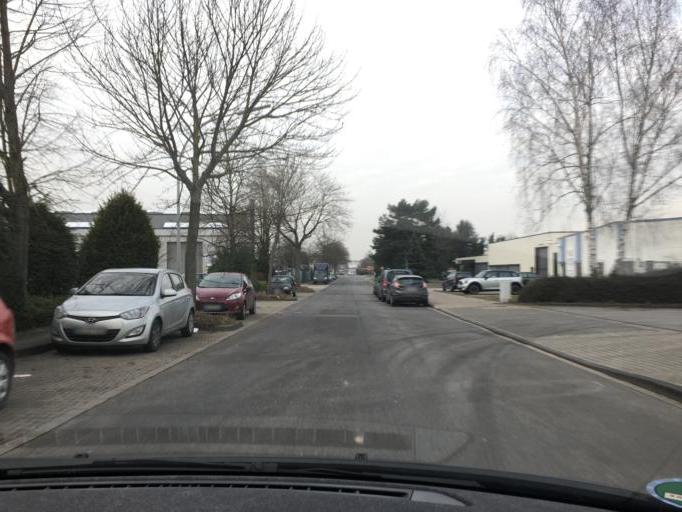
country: DE
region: North Rhine-Westphalia
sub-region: Regierungsbezirk Dusseldorf
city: Monchengladbach
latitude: 51.1375
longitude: 6.4134
